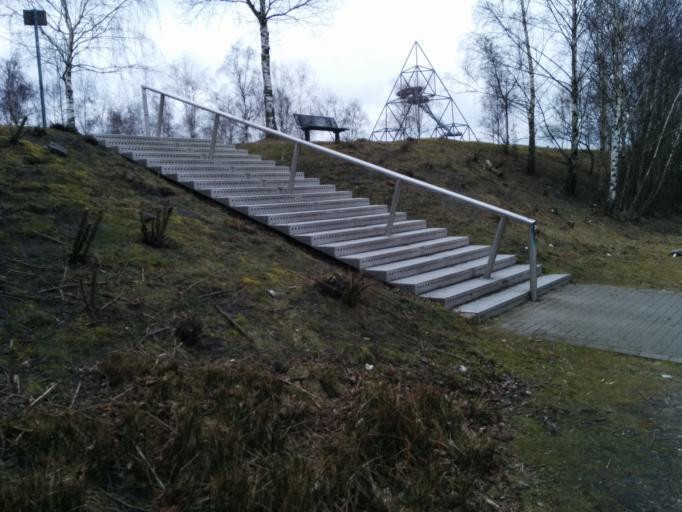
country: DE
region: North Rhine-Westphalia
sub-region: Regierungsbezirk Munster
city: Bottrop
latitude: 51.5254
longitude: 6.9581
